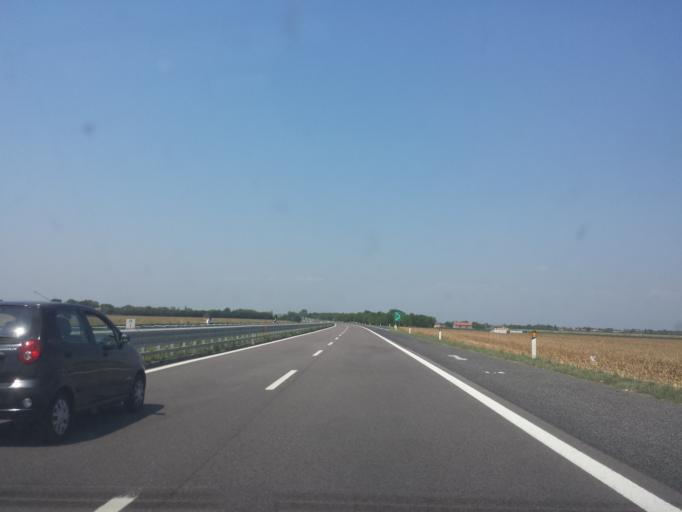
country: IT
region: Veneto
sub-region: Provincia di Venezia
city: Tessera
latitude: 45.5218
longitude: 12.3299
